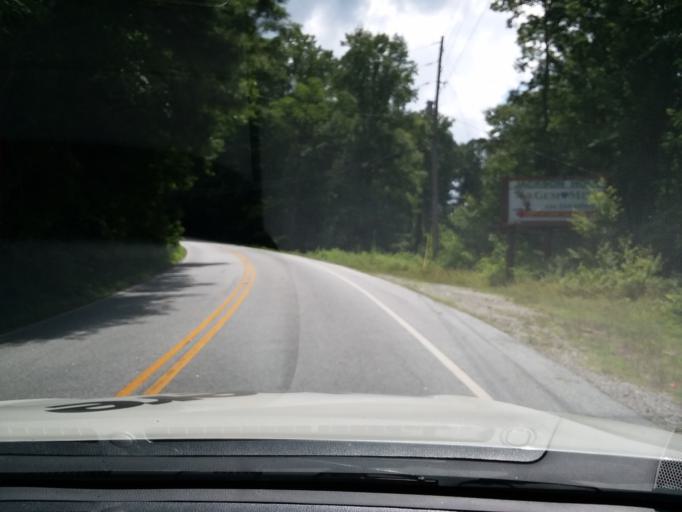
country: US
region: Georgia
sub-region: Rabun County
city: Mountain City
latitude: 35.0213
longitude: -83.2998
